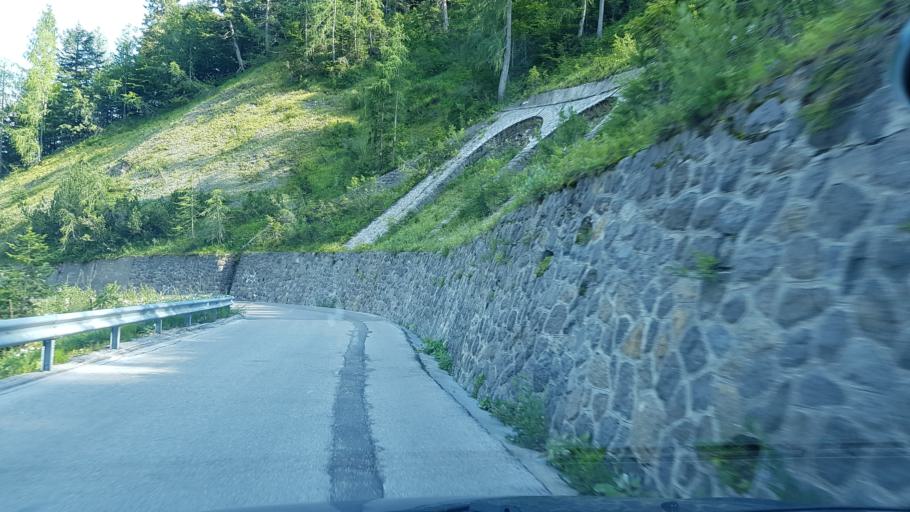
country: IT
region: Friuli Venezia Giulia
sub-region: Provincia di Udine
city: Sauris di Sotto
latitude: 46.4733
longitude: 12.6511
